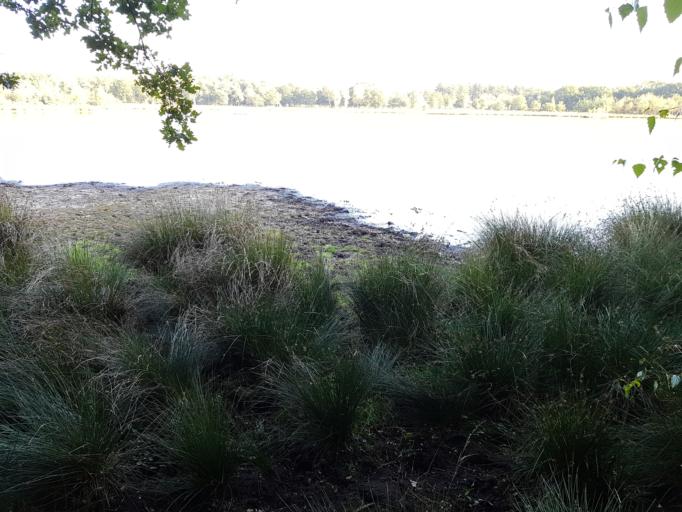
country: NL
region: Utrecht
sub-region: Gemeente Utrechtse Heuvelrug
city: Leersum
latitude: 52.0444
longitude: 5.4393
